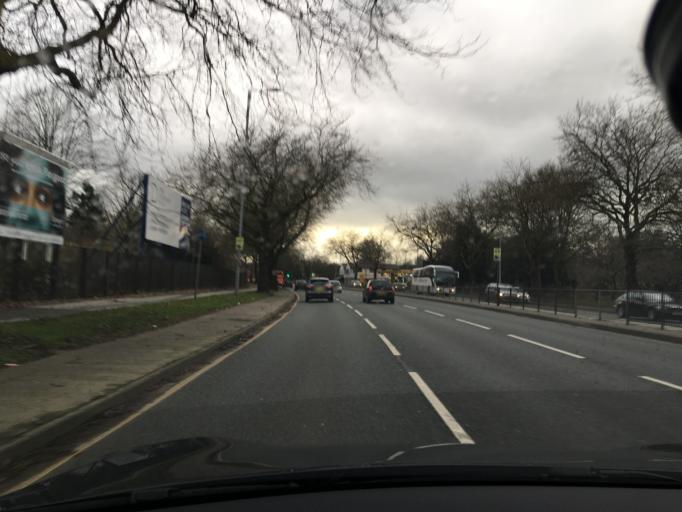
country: GB
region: England
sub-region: Manchester
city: Chorlton cum Hardy
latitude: 53.4304
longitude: -2.2509
